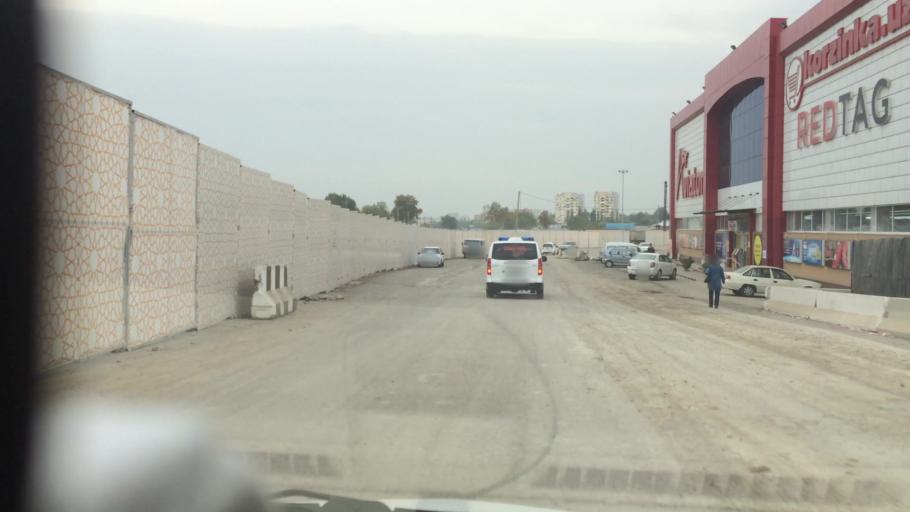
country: UZ
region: Toshkent
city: Salor
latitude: 41.3073
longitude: 69.3379
